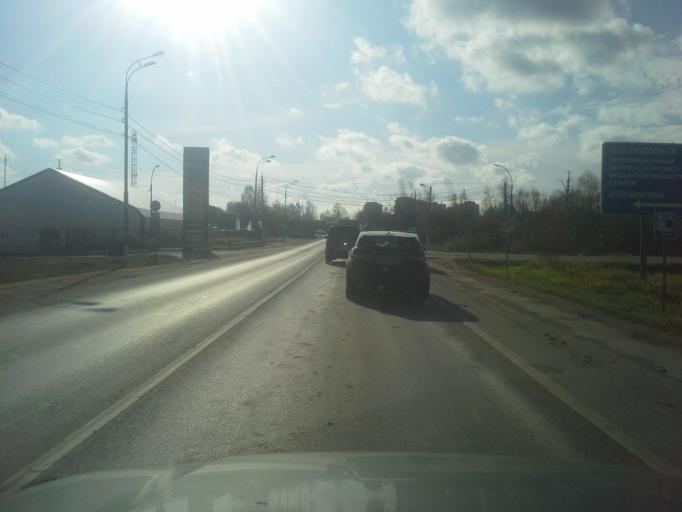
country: RU
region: Moskovskaya
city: Bol'shiye Vyazemy
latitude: 55.6321
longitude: 36.9838
